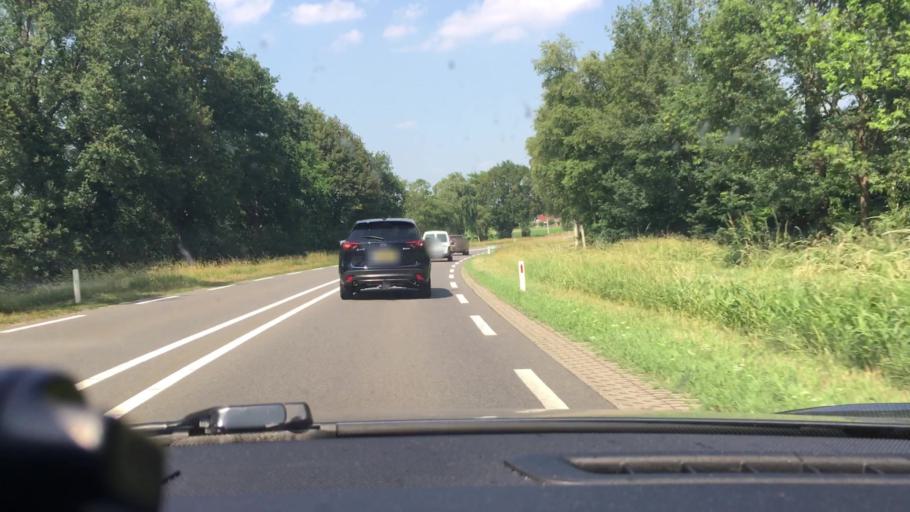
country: NL
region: Overijssel
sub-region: Gemeente Hof van Twente
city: Goor
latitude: 52.2333
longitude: 6.6058
